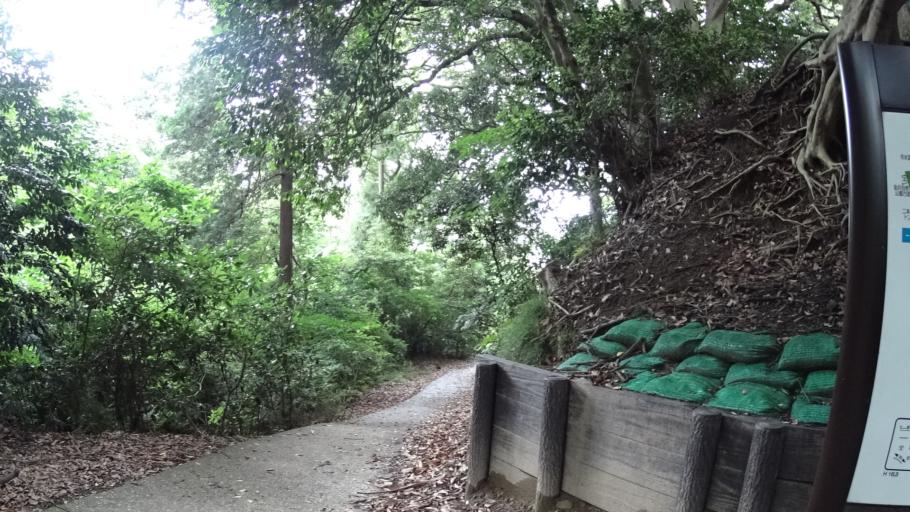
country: JP
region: Kanagawa
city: Zushi
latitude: 35.3503
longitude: 139.6182
